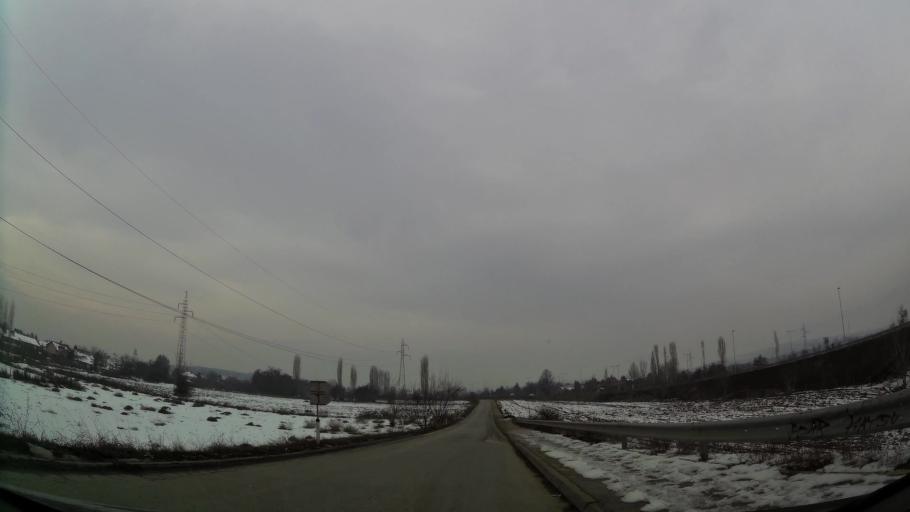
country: MK
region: Butel
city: Butel
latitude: 42.0398
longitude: 21.4544
